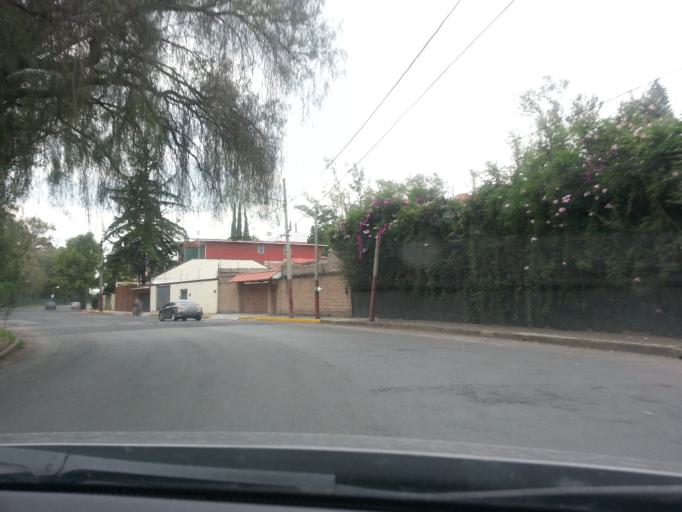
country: MX
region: Mexico
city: Ciudad Lopez Mateos
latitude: 19.6181
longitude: -99.2448
